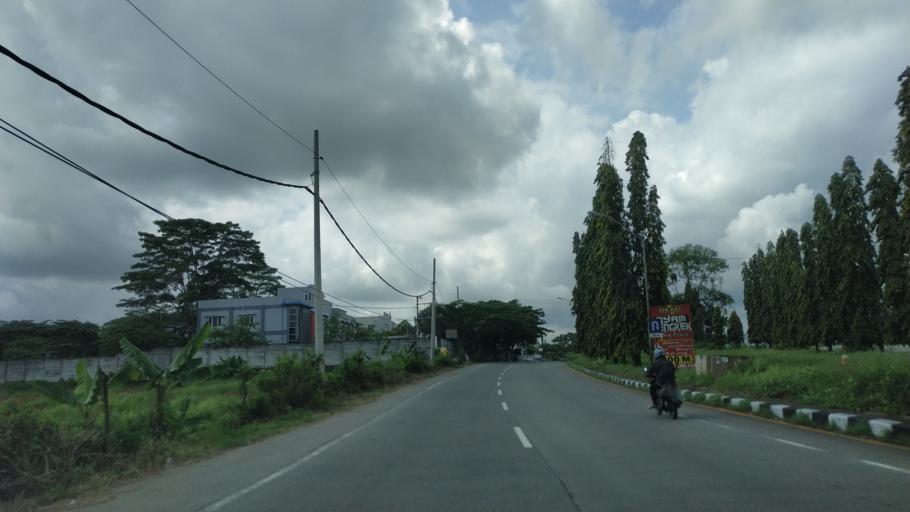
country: ID
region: Central Java
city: Pekalongan
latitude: -6.9477
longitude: 109.8253
